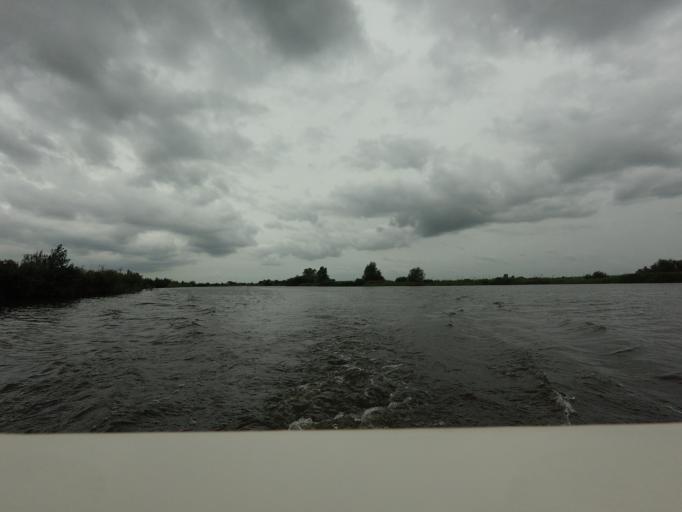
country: NL
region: Friesland
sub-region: Gemeente Boarnsterhim
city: Aldeboarn
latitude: 53.0952
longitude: 5.9255
